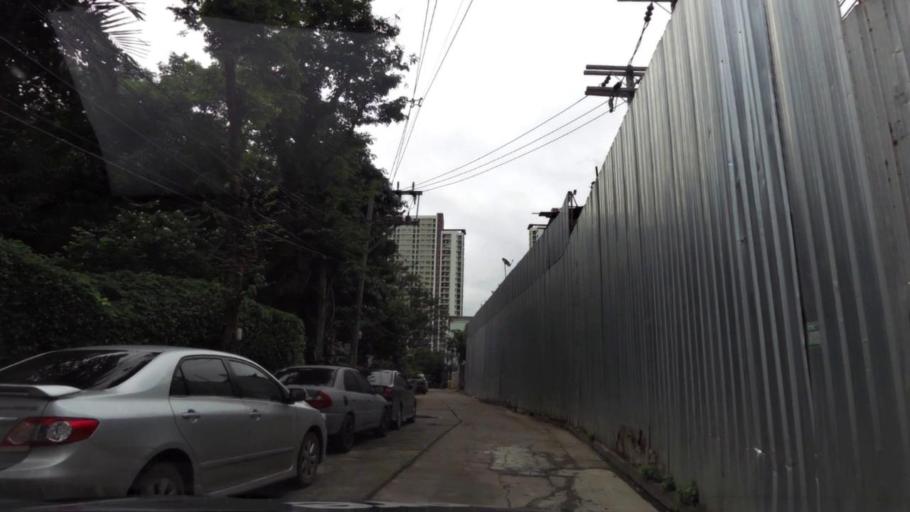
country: TH
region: Bangkok
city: Din Daeng
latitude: 13.7584
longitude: 100.5689
